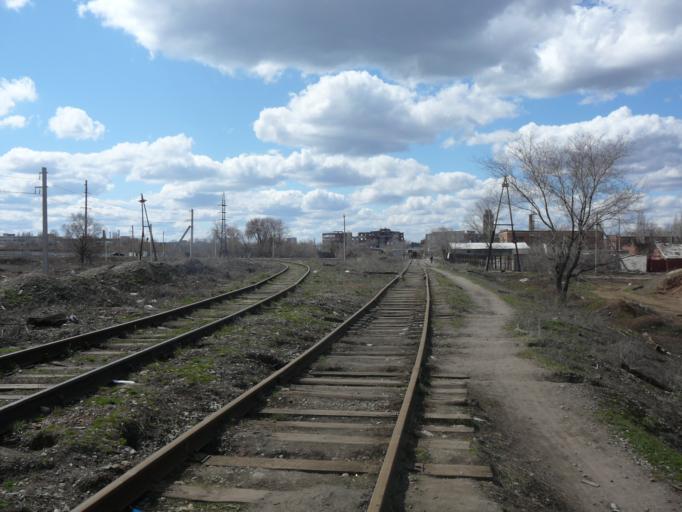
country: RU
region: Saratov
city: Privolzhskiy
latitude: 51.4129
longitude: 46.0643
